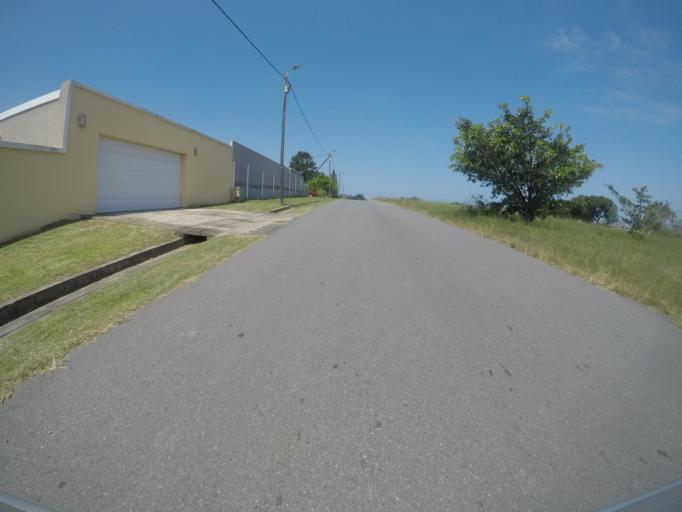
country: ZA
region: Eastern Cape
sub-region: Buffalo City Metropolitan Municipality
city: East London
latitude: -32.9727
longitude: 27.8750
